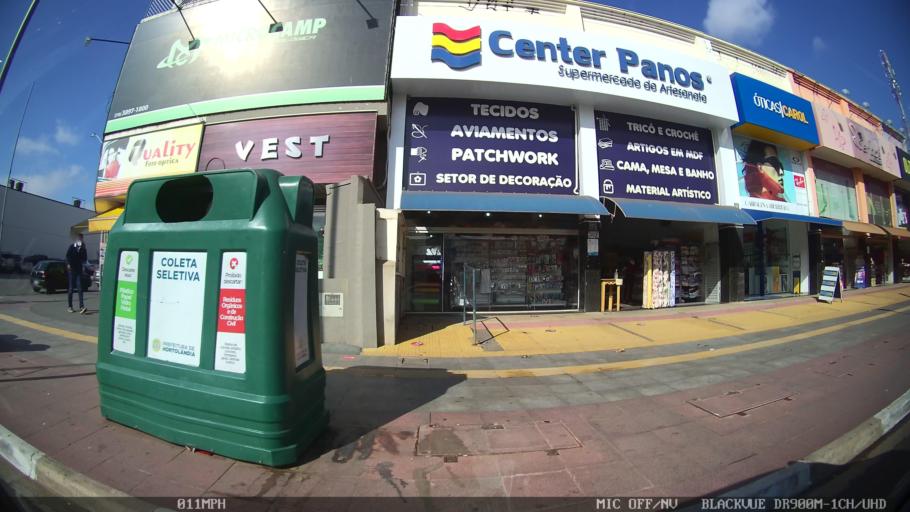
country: BR
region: Sao Paulo
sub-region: Hortolandia
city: Hortolandia
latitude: -22.8644
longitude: -47.2149
